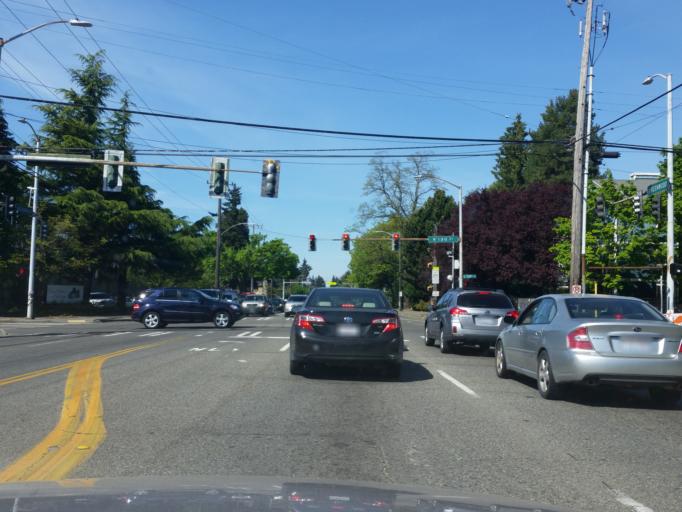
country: US
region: Washington
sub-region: King County
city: Shoreline
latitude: 47.7230
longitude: -122.3555
